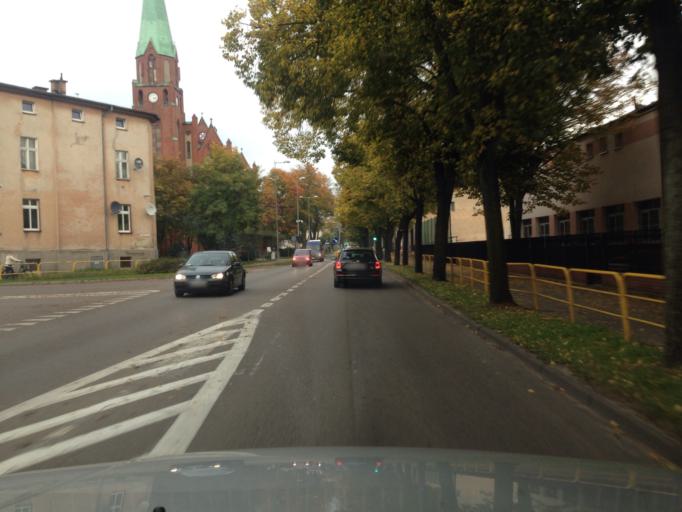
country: PL
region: Pomeranian Voivodeship
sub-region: Powiat leborski
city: Lebork
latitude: 54.5443
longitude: 17.7465
